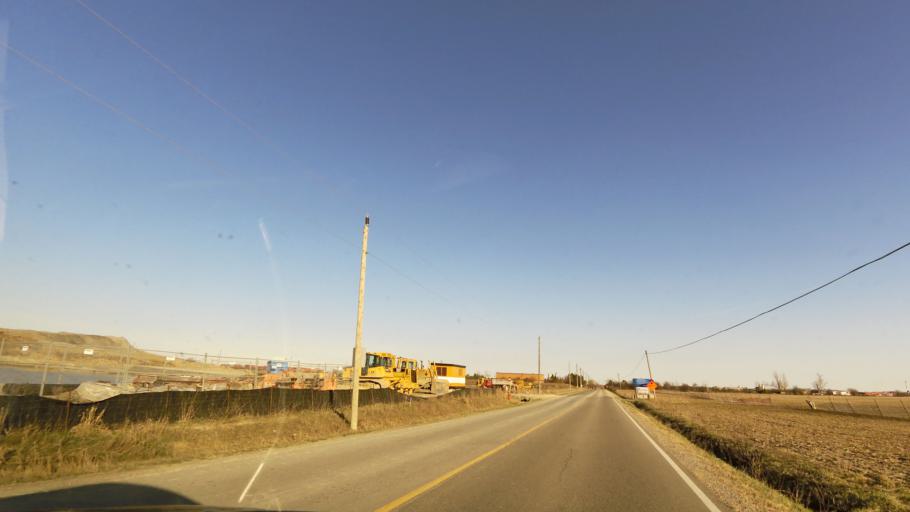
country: CA
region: Ontario
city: Brampton
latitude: 43.8249
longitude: -79.6870
